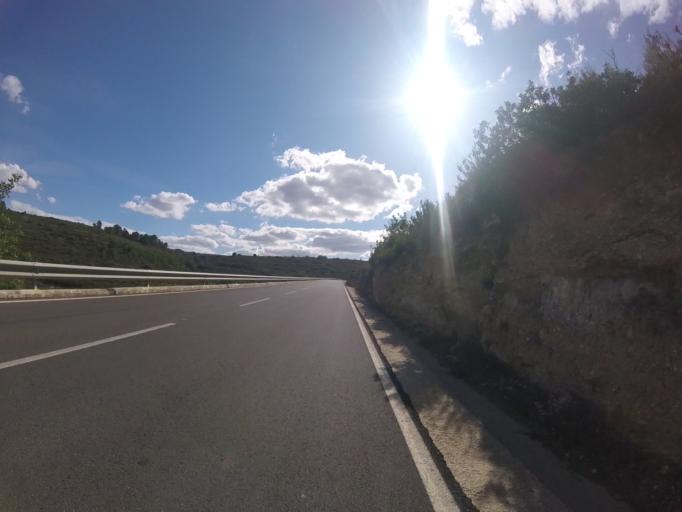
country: ES
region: Valencia
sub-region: Provincia de Castello
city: Cuevas de Vinroma
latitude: 40.3164
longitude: 0.1343
